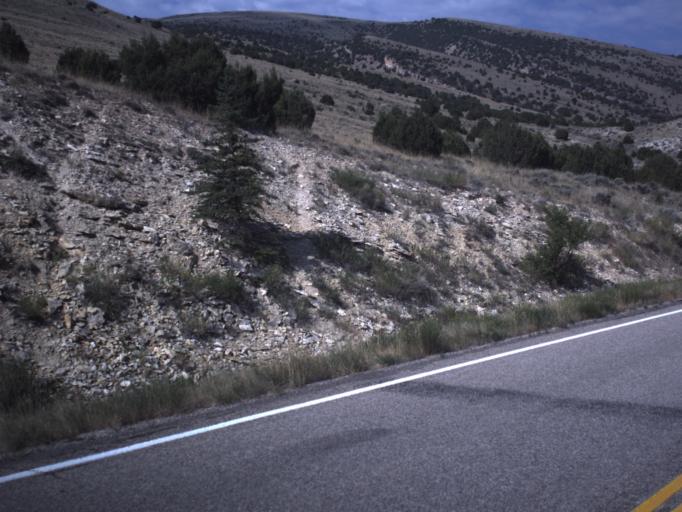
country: US
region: Utah
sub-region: Daggett County
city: Manila
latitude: 40.9165
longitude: -109.6897
